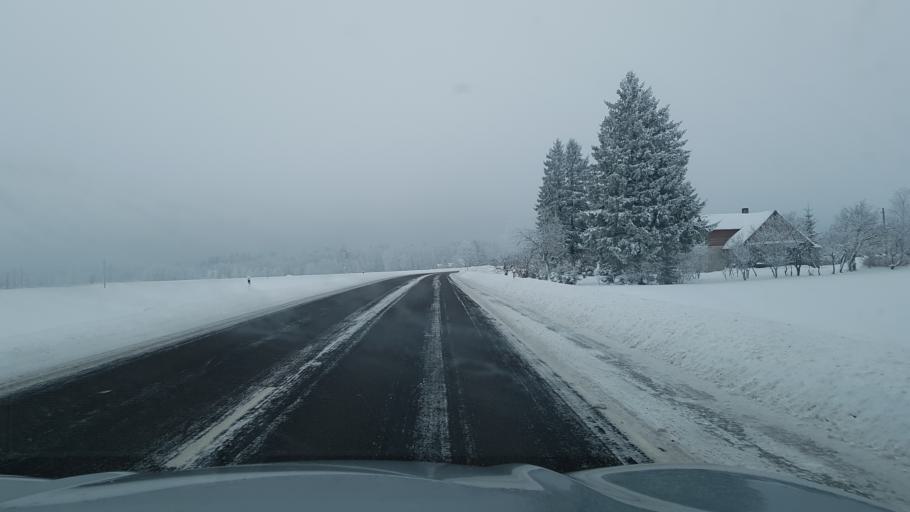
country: EE
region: Ida-Virumaa
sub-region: Johvi vald
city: Johvi
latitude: 59.2679
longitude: 27.3842
